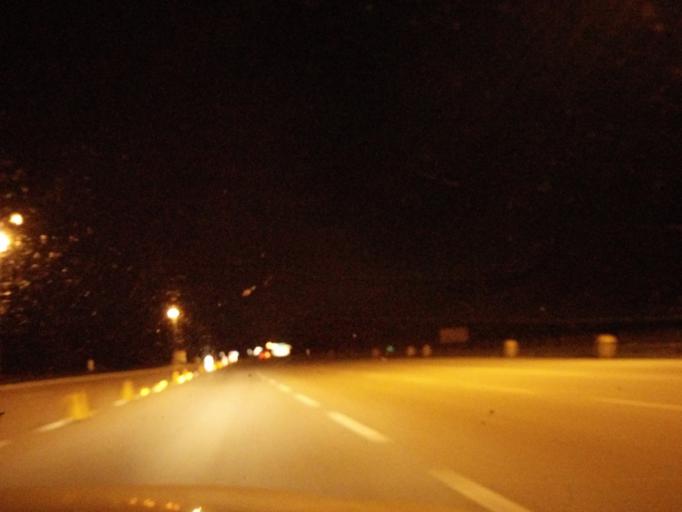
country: HR
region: Vukovarsko-Srijemska
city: Nijemci
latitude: 45.0468
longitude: 19.0234
